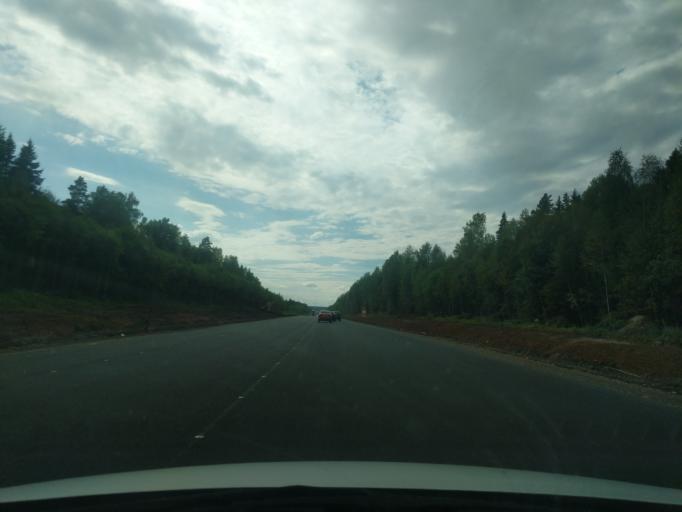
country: RU
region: Kostroma
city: Sudislavl'
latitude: 57.8251
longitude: 41.4996
